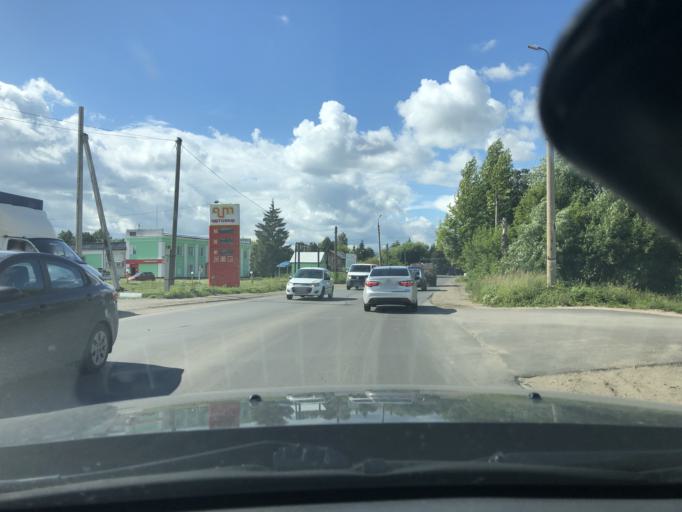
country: RU
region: Tula
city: Donskoy
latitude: 53.9683
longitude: 38.3585
